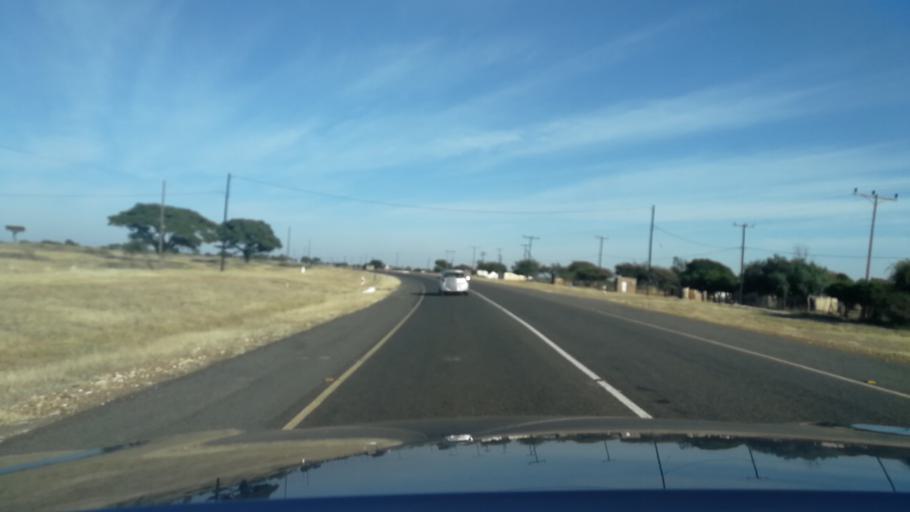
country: BW
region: South East
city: Janeng
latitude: -25.4679
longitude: 25.5415
